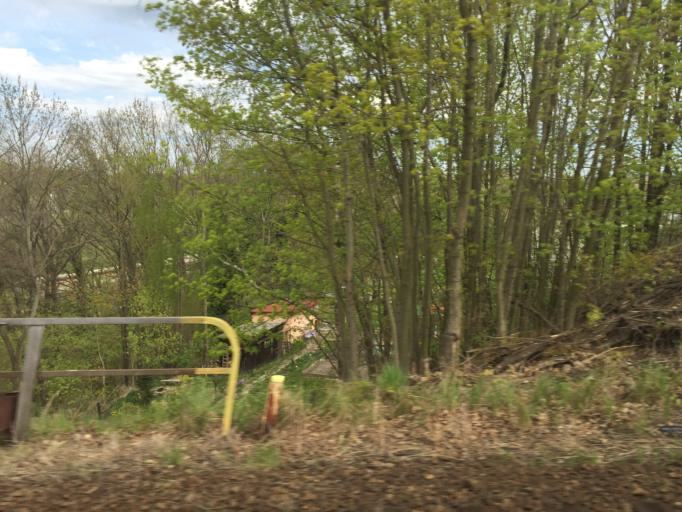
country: DE
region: Saxony
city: Lobau
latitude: 51.0982
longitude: 14.6787
